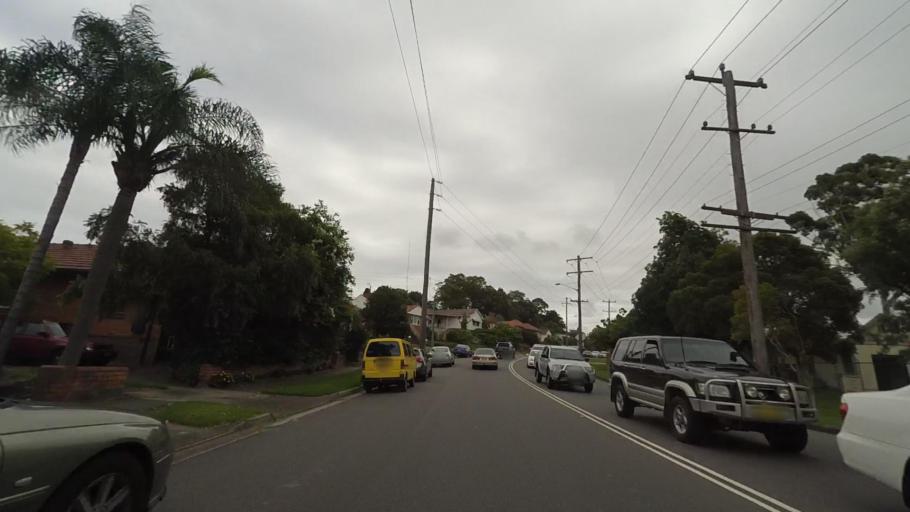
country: AU
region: New South Wales
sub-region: Lake Macquarie Shire
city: Highfields
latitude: -32.9422
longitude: 151.7048
